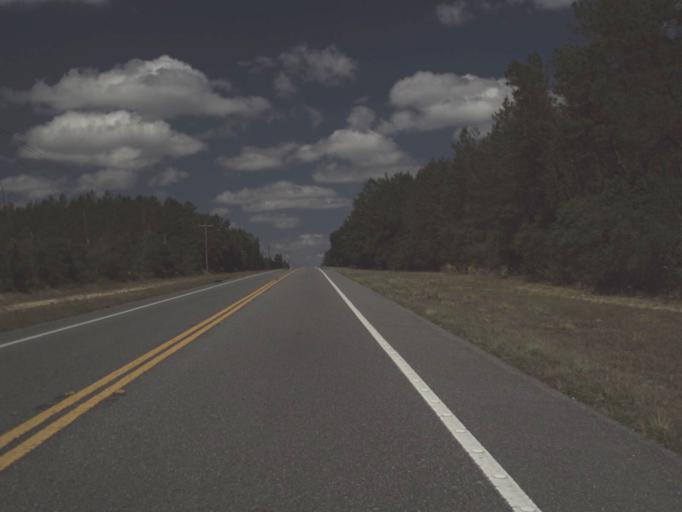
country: US
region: Florida
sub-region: Lake County
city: Astor
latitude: 29.1779
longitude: -81.7346
